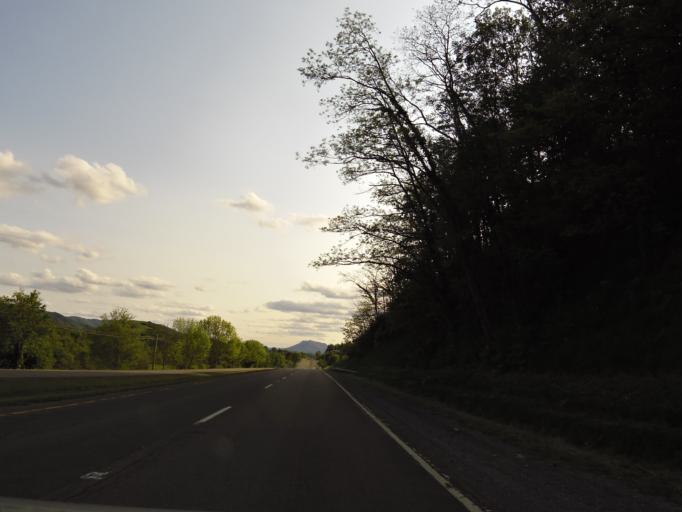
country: US
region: Virginia
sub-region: Tazewell County
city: Springville
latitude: 37.1717
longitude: -81.4500
